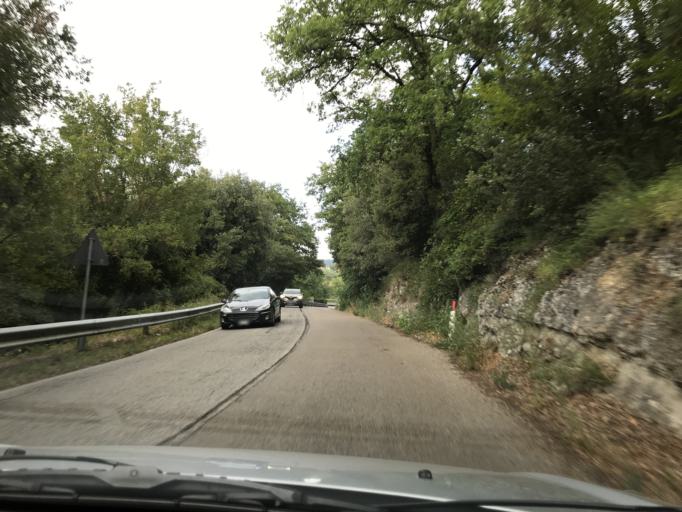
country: IT
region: Umbria
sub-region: Provincia di Terni
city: Montecchio
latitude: 42.6543
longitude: 12.2803
